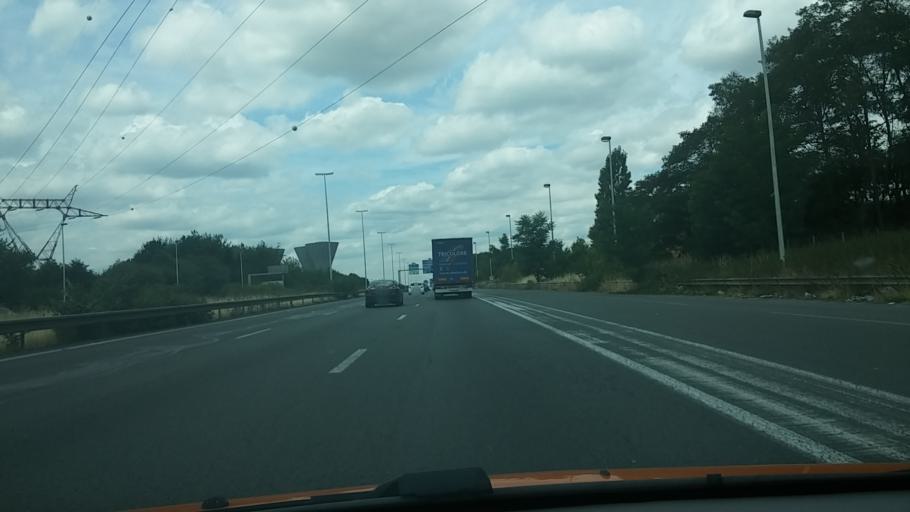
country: FR
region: Ile-de-France
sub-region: Departement de Seine-Saint-Denis
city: Villepinte
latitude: 48.9665
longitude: 2.5149
